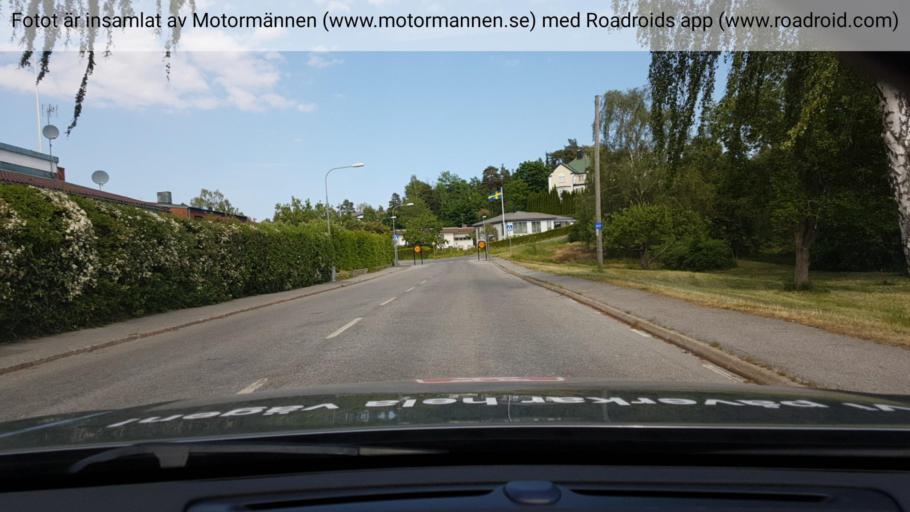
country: SE
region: Stockholm
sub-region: Lidingo
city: Brevik
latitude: 59.3497
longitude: 18.2250
